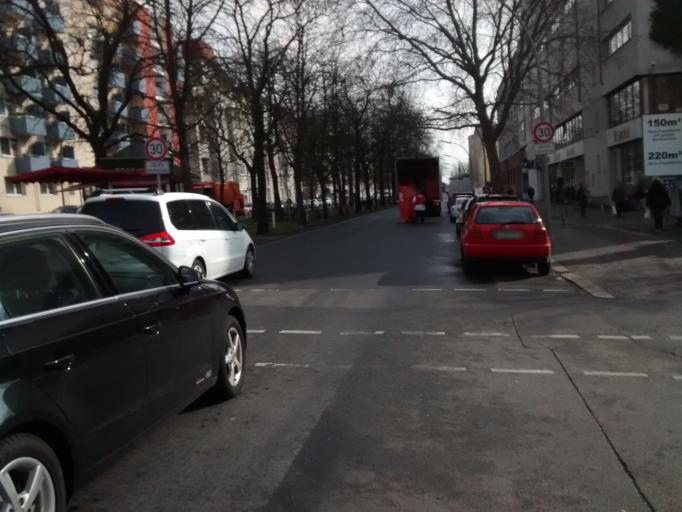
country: DE
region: Berlin
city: Moabit
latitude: 52.5213
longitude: 13.3336
